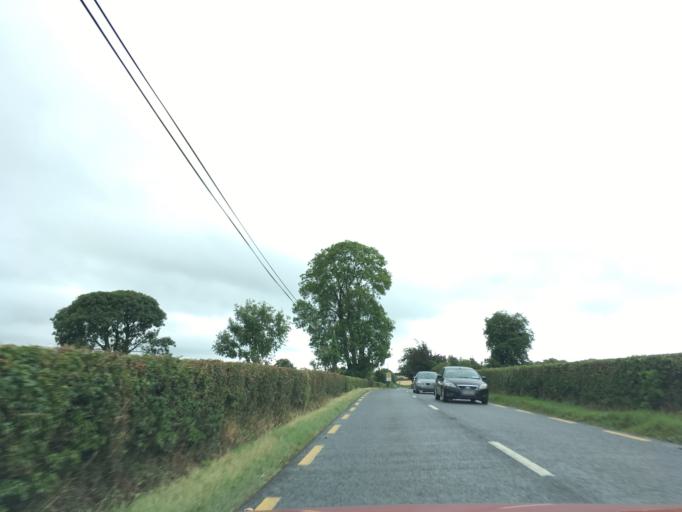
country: IE
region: Munster
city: Fethard
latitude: 52.4258
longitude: -7.7743
